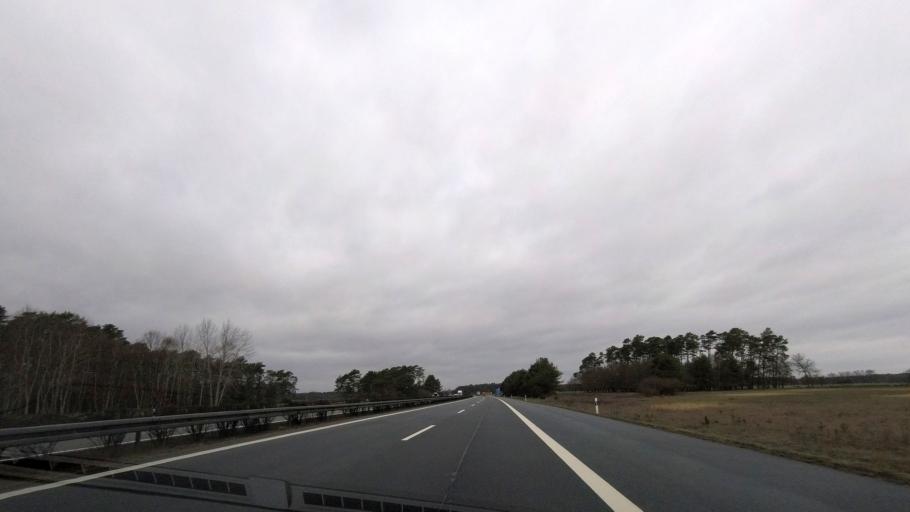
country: DE
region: Mecklenburg-Vorpommern
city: Sulstorf
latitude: 53.4584
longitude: 11.3514
